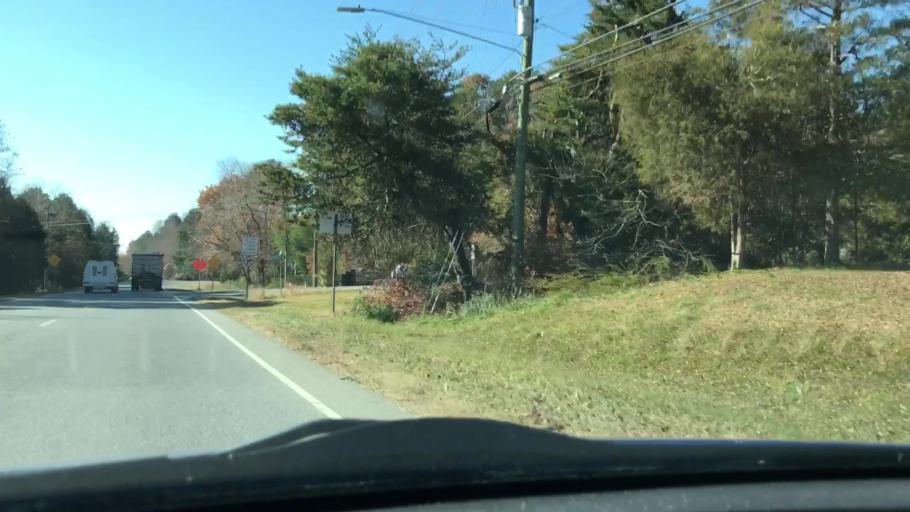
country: US
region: North Carolina
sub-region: Randolph County
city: Asheboro
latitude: 35.6823
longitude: -79.8455
